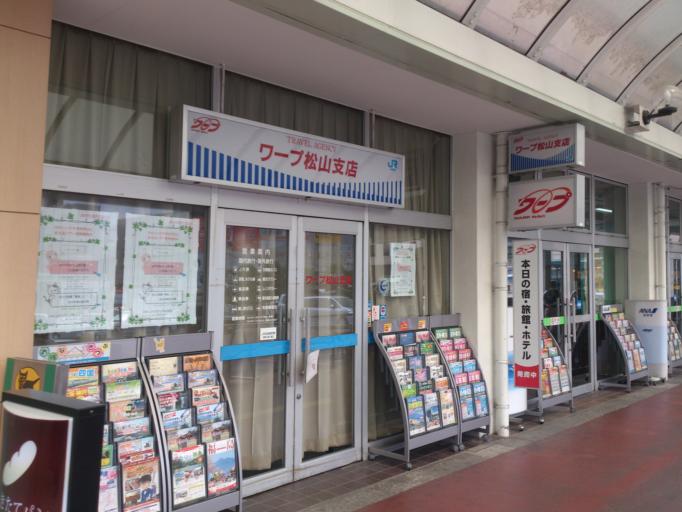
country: JP
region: Ehime
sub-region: Shikoku-chuo Shi
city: Matsuyama
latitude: 33.8401
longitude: 132.7517
